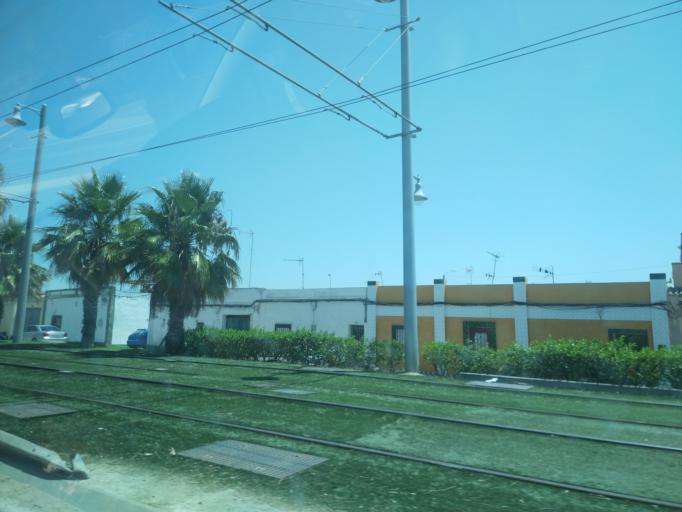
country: ES
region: Andalusia
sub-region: Provincia de Cadiz
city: San Fernando
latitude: 36.4691
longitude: -6.1874
